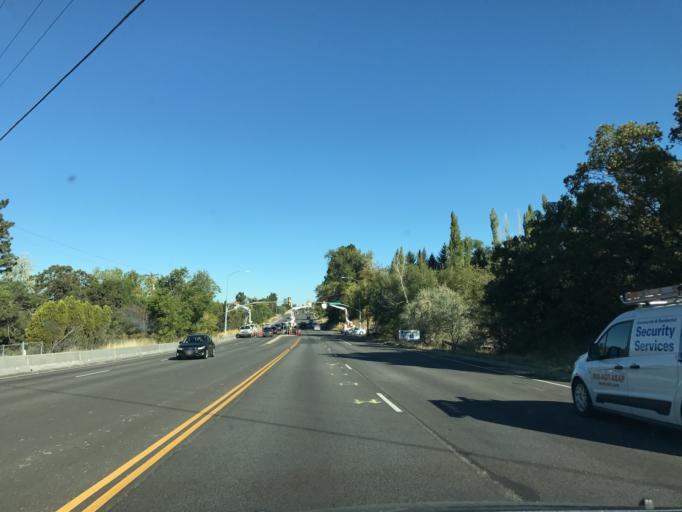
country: US
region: Utah
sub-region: Weber County
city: Uintah
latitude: 41.1673
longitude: -111.9442
